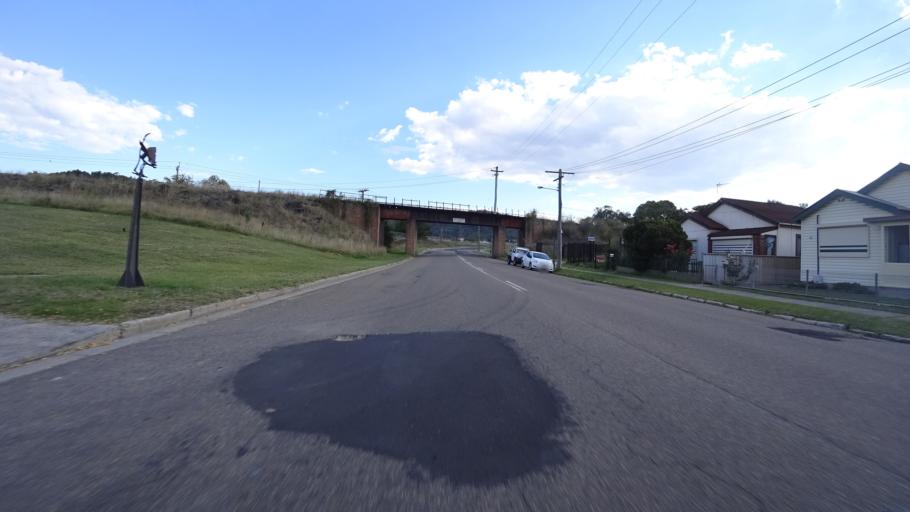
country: AU
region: New South Wales
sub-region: Lithgow
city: Lithgow
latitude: -33.4765
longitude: 150.1675
